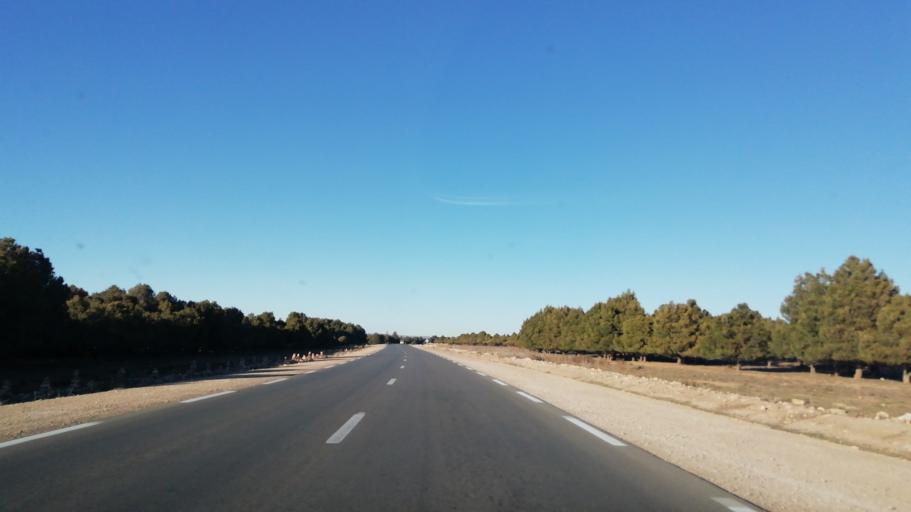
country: DZ
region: Tlemcen
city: Sebdou
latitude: 34.4546
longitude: -1.2753
